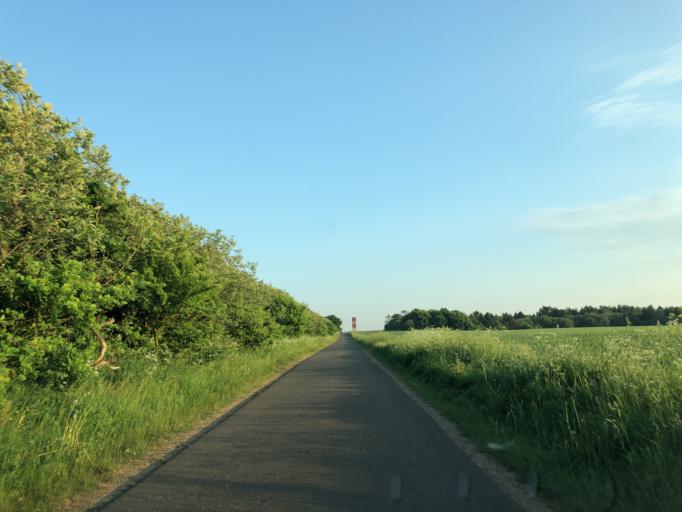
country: DK
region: Central Jutland
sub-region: Struer Kommune
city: Struer
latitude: 56.4125
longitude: 8.4886
